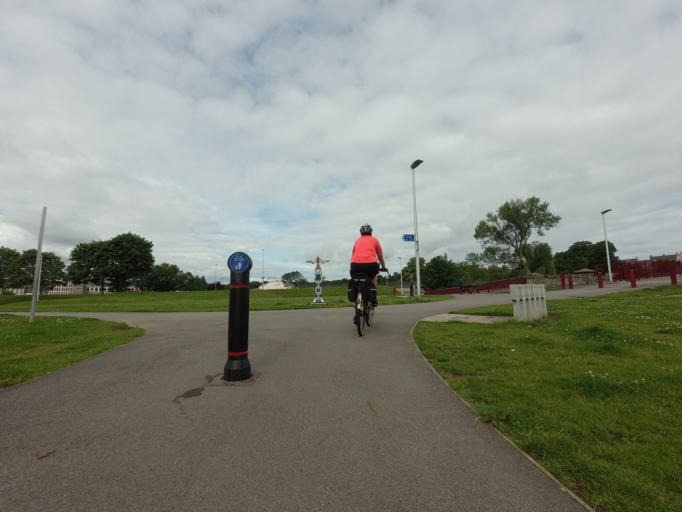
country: GB
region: Scotland
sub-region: Moray
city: Elgin
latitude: 57.6522
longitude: -3.3151
